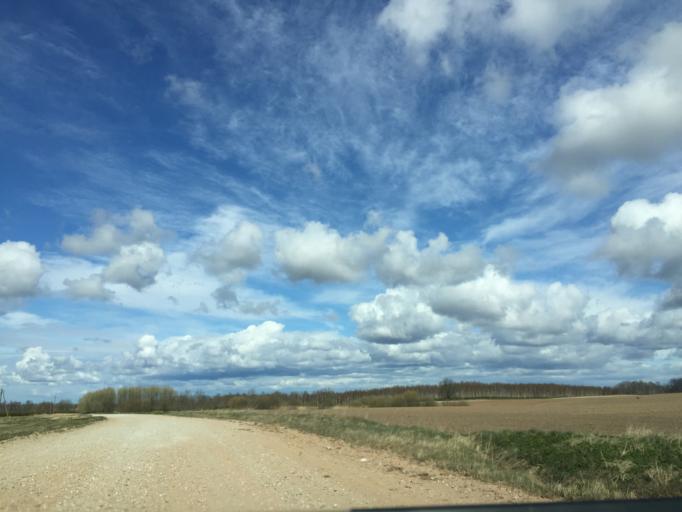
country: LV
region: Limbazu Rajons
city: Limbazi
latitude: 57.5862
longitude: 24.5983
